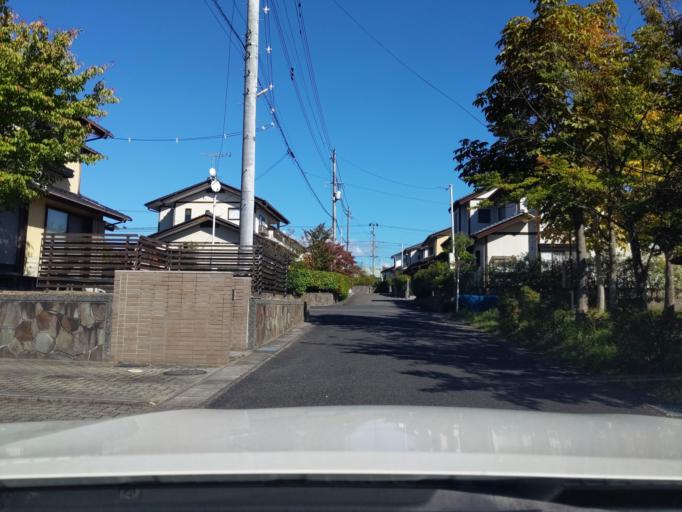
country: JP
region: Fukushima
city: Koriyama
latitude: 37.3821
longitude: 140.4335
